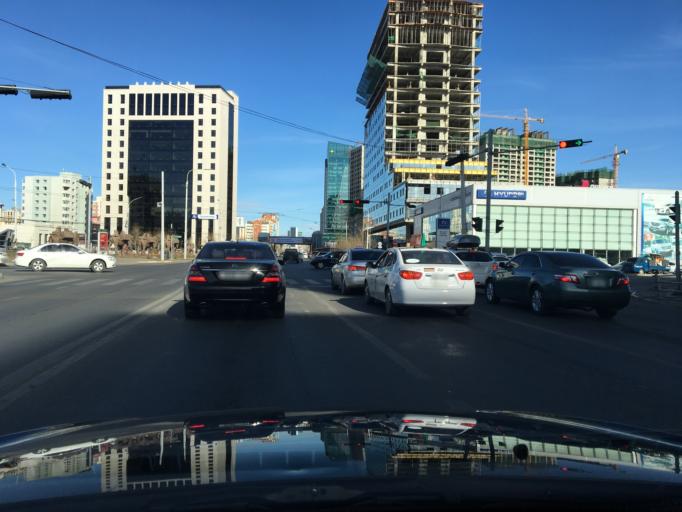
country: MN
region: Ulaanbaatar
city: Ulaanbaatar
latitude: 47.8990
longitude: 106.9091
